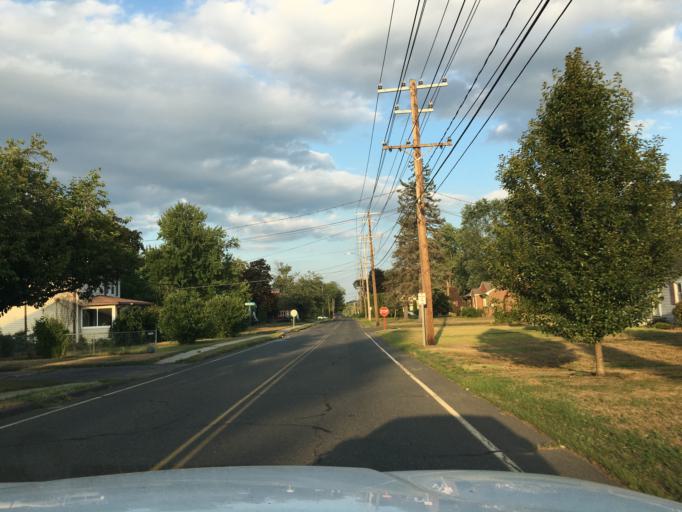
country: US
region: Connecticut
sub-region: Hartford County
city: Windsor Locks
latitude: 41.9196
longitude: -72.6317
